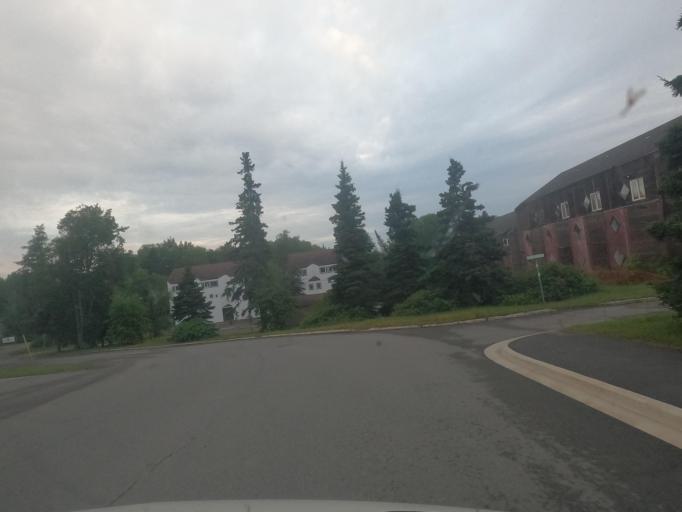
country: CA
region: Ontario
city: Marathon
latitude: 48.7803
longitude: -87.1027
